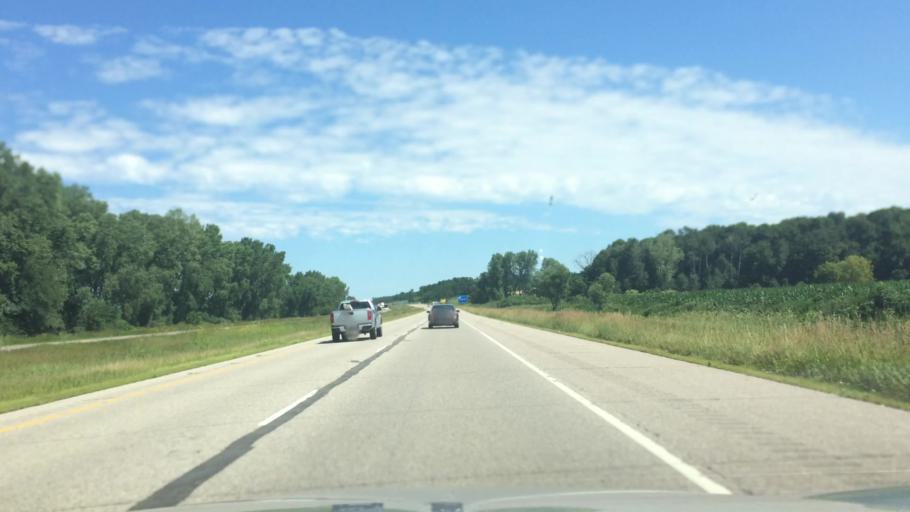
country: US
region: Wisconsin
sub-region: Columbia County
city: Portage
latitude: 43.6881
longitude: -89.4696
